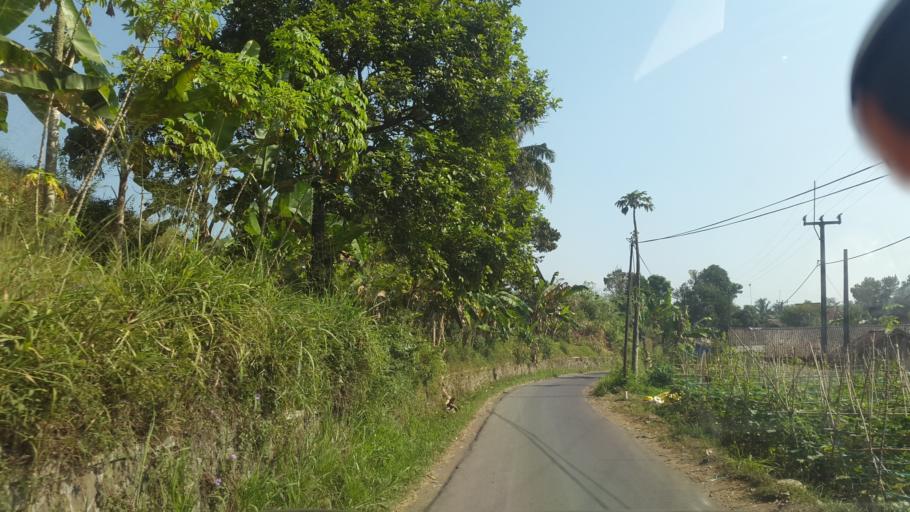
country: ID
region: West Java
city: Cicurug
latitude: -6.8537
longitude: 106.8018
